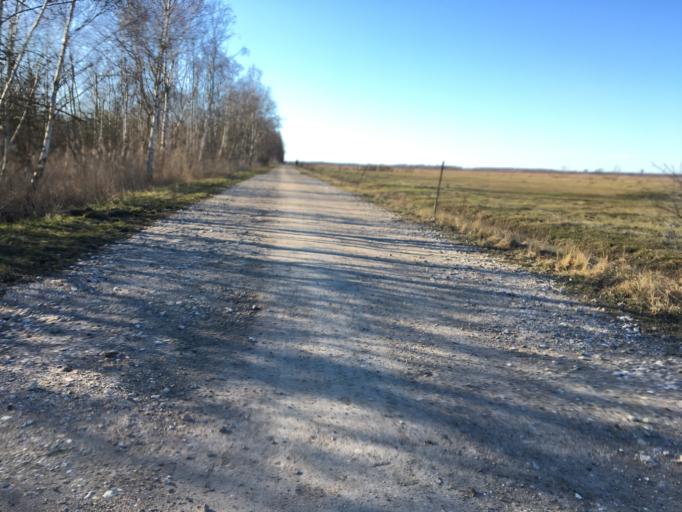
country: DK
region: Capital Region
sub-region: Tarnby Kommune
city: Tarnby
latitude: 55.5947
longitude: 12.5671
